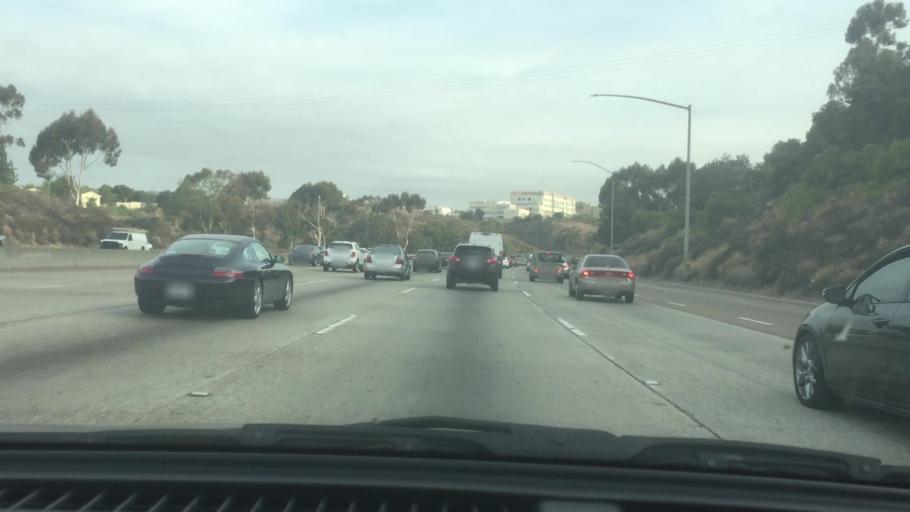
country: US
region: California
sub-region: San Diego County
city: San Diego
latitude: 32.7900
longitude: -117.1488
